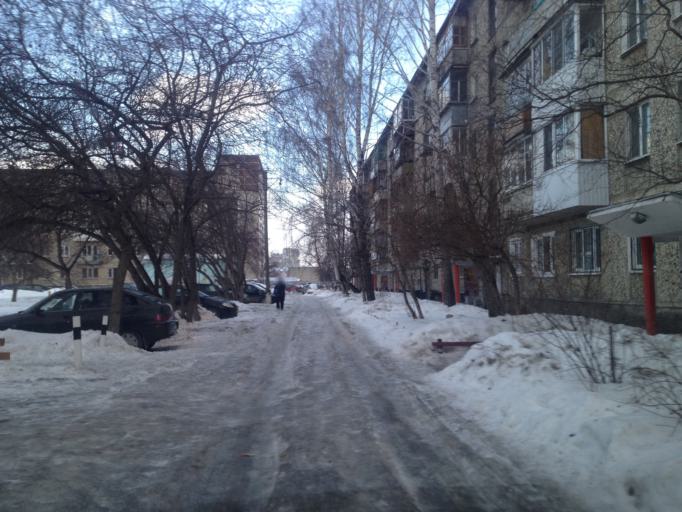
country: RU
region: Sverdlovsk
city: Yekaterinburg
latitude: 56.9067
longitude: 60.6011
